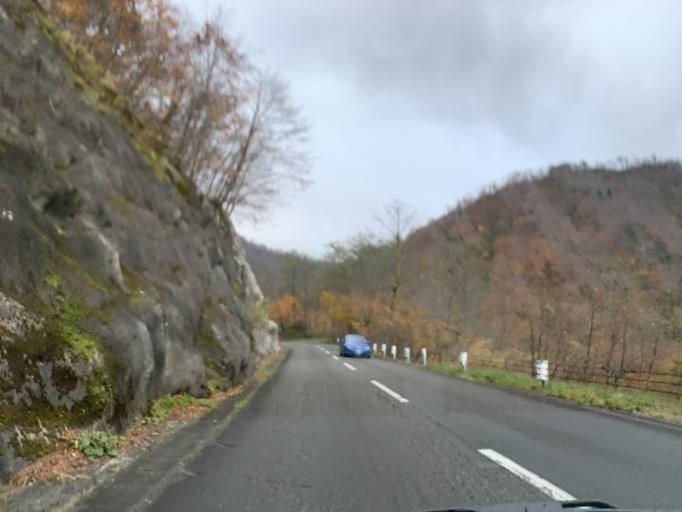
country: JP
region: Iwate
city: Mizusawa
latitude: 39.1203
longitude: 140.8328
